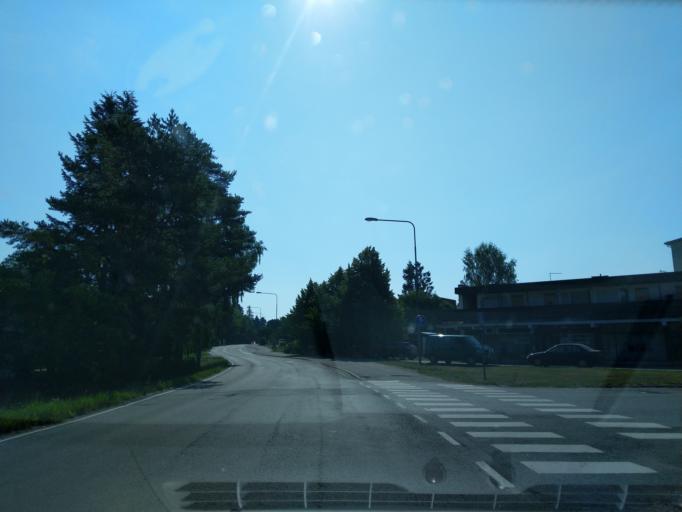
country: FI
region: Satakunta
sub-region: Pori
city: Noormarkku
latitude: 61.5930
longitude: 21.8719
